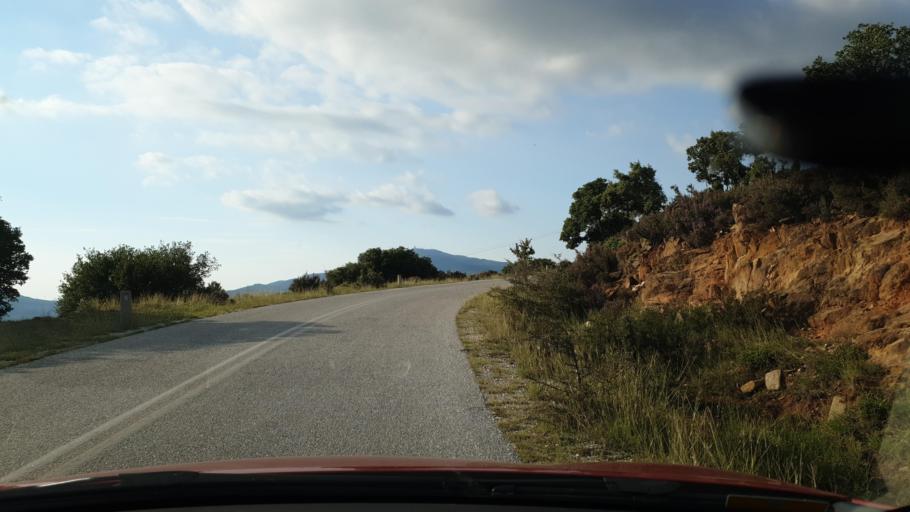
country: GR
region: Central Macedonia
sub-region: Nomos Thessalonikis
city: Peristera
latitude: 40.5141
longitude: 23.1732
